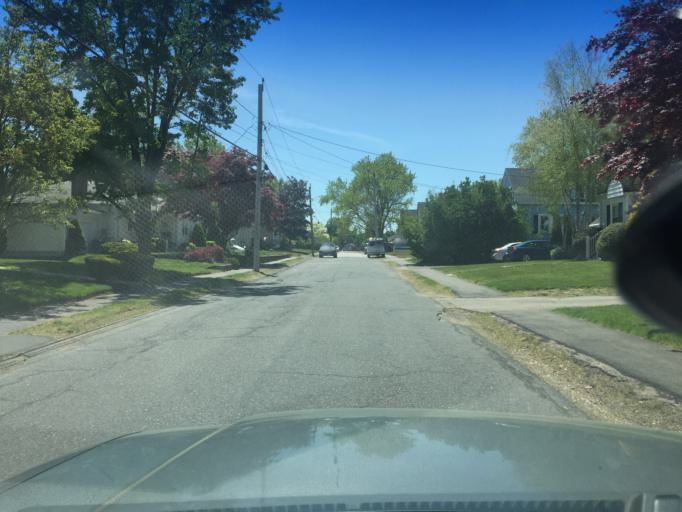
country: US
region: Massachusetts
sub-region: Norfolk County
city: Norwood
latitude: 42.1929
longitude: -71.1884
